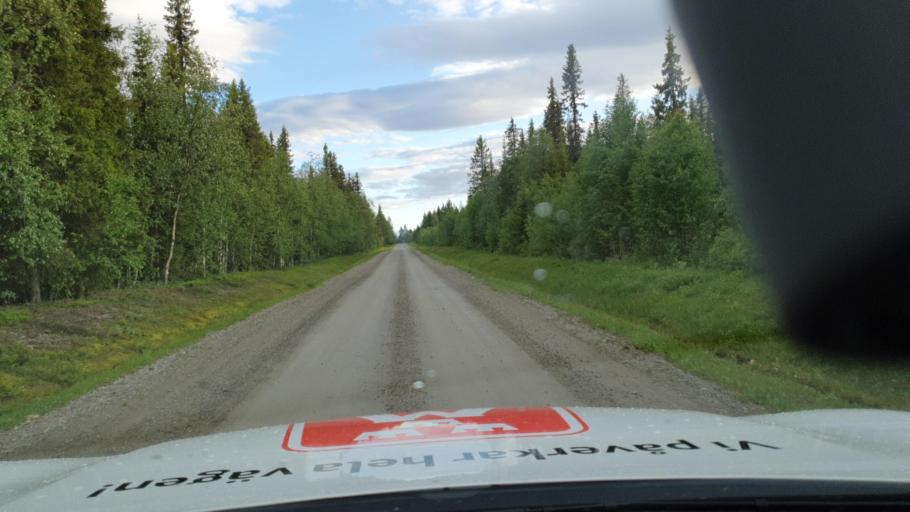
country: SE
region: Vaesterbotten
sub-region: Storumans Kommun
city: Storuman
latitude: 64.7416
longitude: 17.0731
